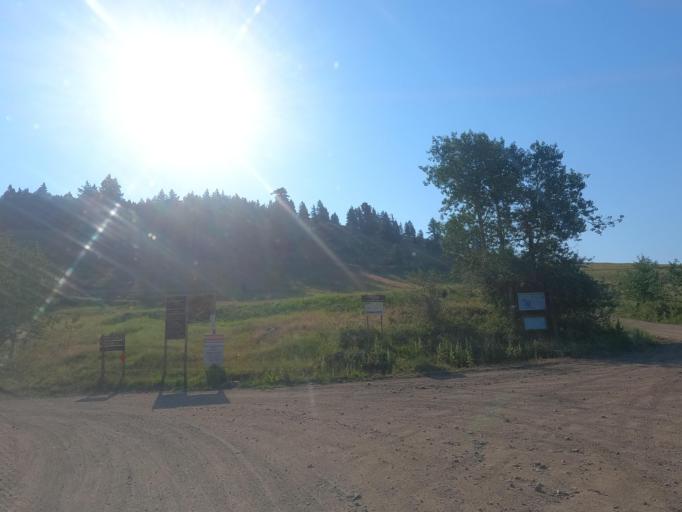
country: CA
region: British Columbia
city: Merritt
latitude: 50.0669
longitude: -120.6593
